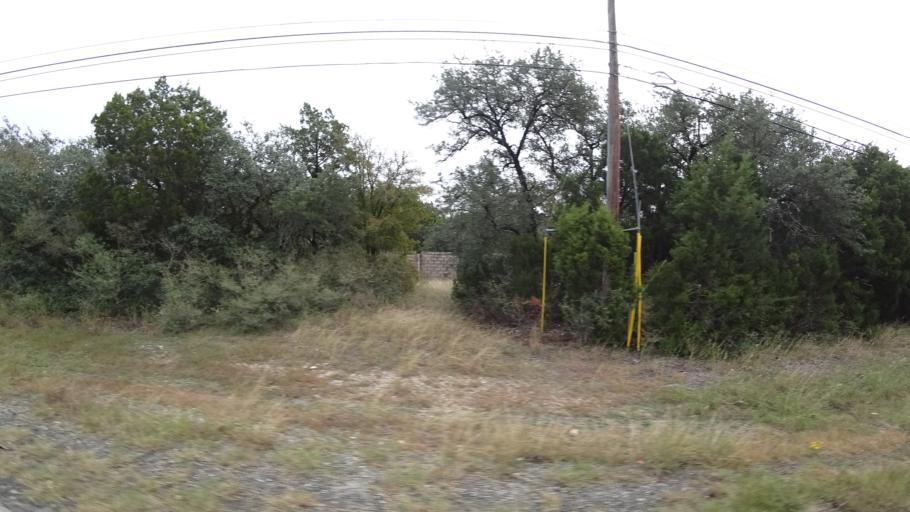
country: US
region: Texas
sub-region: Travis County
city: Barton Creek
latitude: 30.2250
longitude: -97.8908
